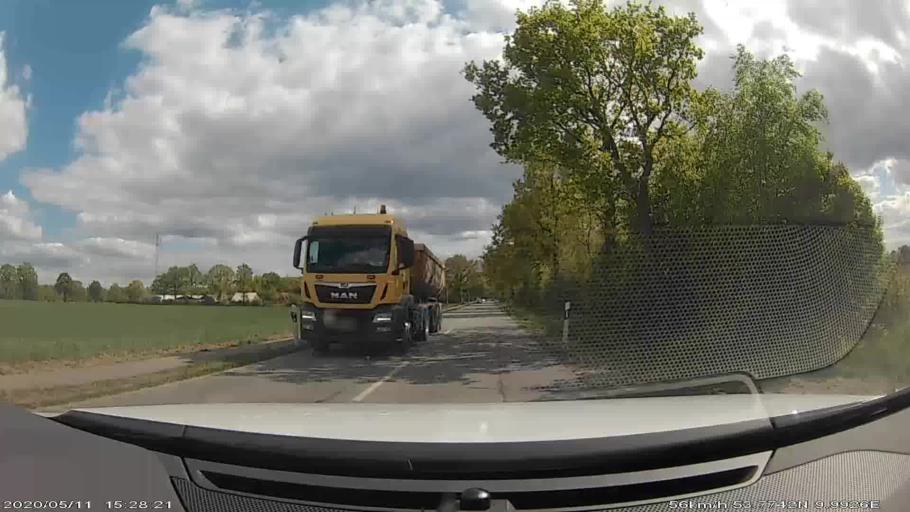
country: DE
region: Schleswig-Holstein
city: Henstedt-Ulzburg
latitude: 53.7641
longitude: 9.9973
